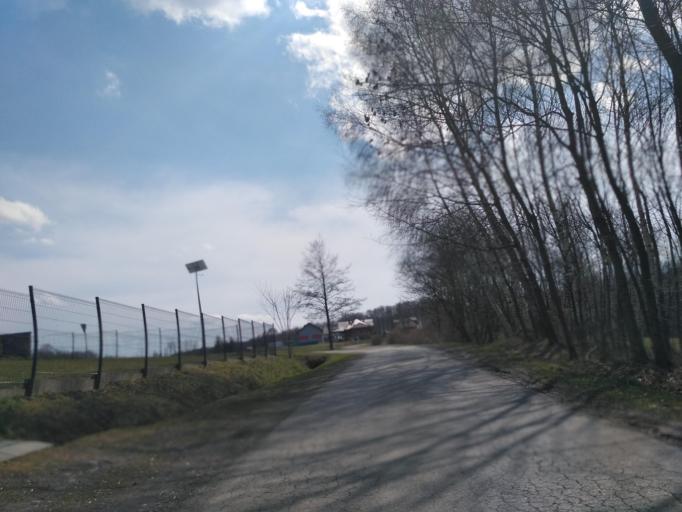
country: PL
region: Subcarpathian Voivodeship
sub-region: Powiat ropczycko-sedziszowski
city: Sedziszow Malopolski
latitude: 50.0443
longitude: 21.7209
